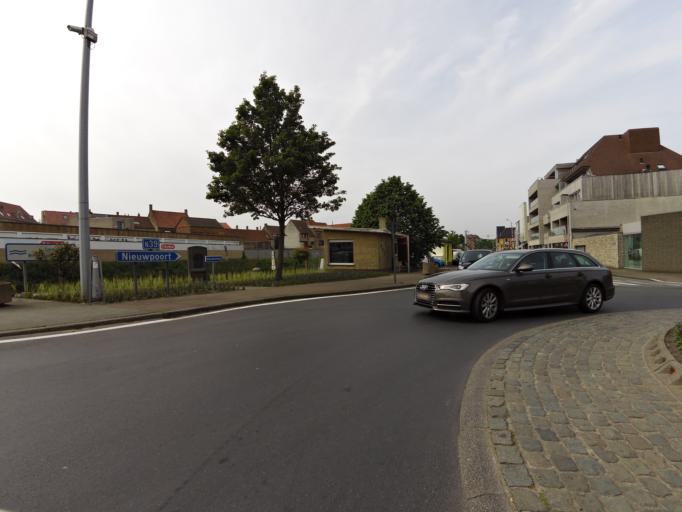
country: BE
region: Flanders
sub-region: Provincie West-Vlaanderen
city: Veurne
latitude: 51.0732
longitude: 2.6679
